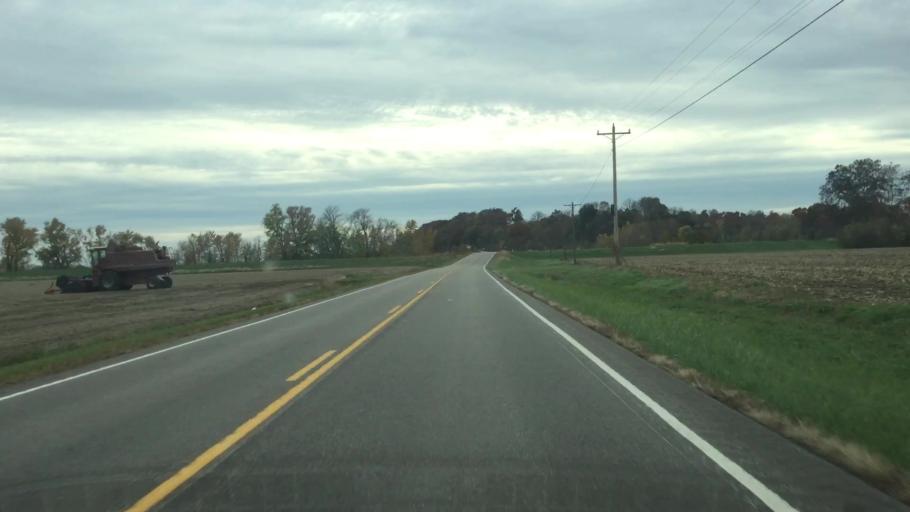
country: US
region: Missouri
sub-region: Callaway County
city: Fulton
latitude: 38.6985
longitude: -91.8236
